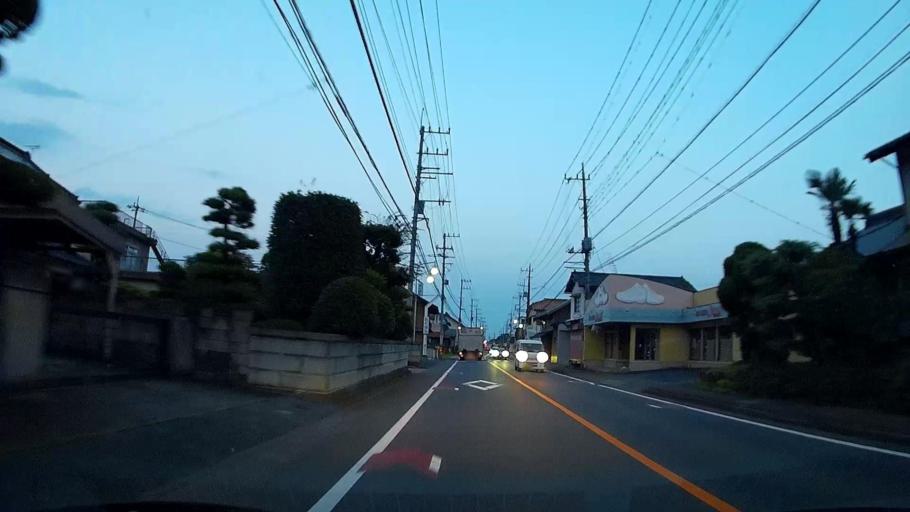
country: JP
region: Gunma
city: Annaka
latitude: 36.3781
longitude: 138.8883
